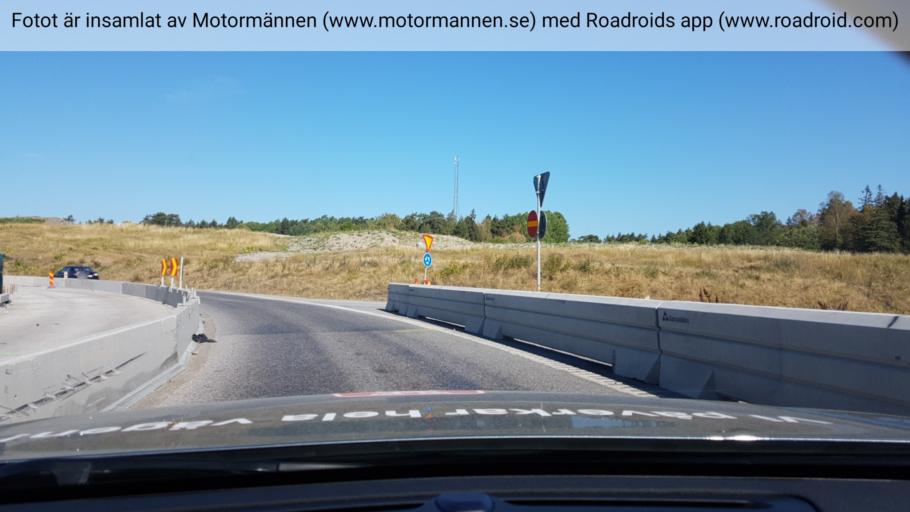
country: SE
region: Stockholm
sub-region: Jarfalla Kommun
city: Jakobsberg
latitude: 59.4012
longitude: 17.8850
